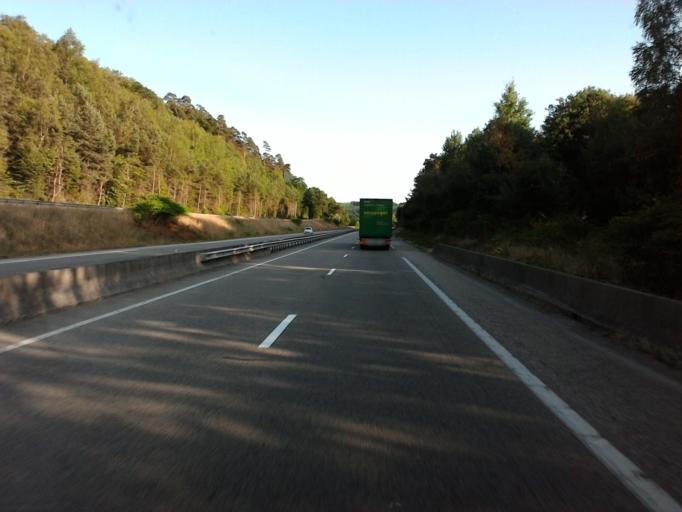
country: FR
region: Lorraine
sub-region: Departement des Vosges
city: Arches
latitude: 48.1365
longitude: 6.5147
